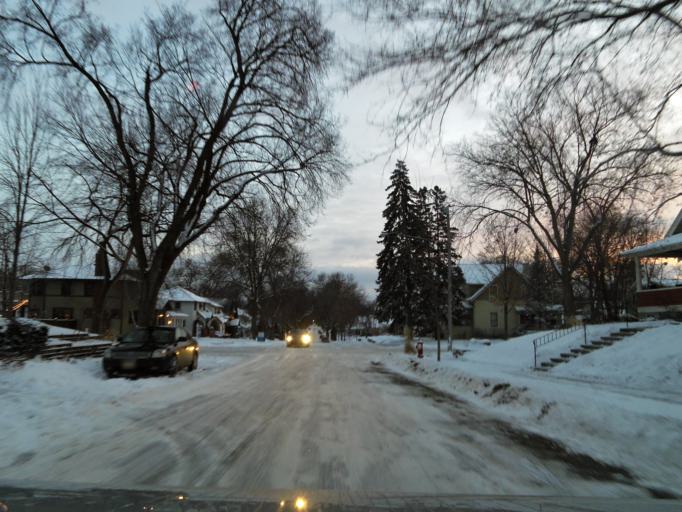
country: US
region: Minnesota
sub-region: Hennepin County
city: Saint Louis Park
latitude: 44.9201
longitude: -93.3215
